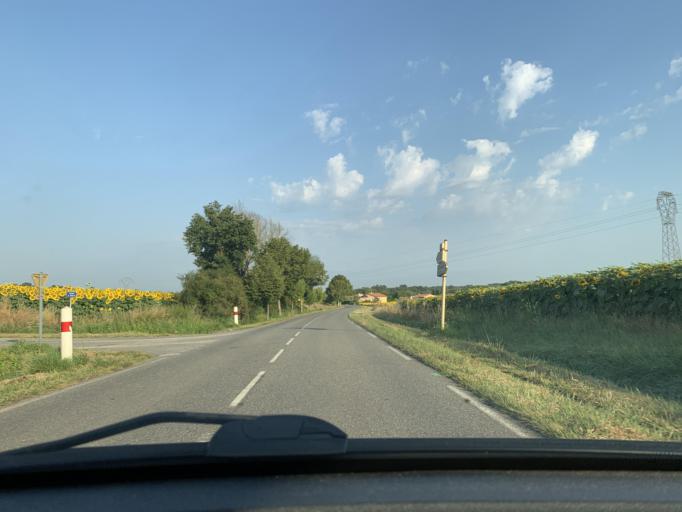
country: FR
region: Midi-Pyrenees
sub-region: Departement de la Haute-Garonne
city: Escalquens
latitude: 43.5282
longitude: 1.5599
